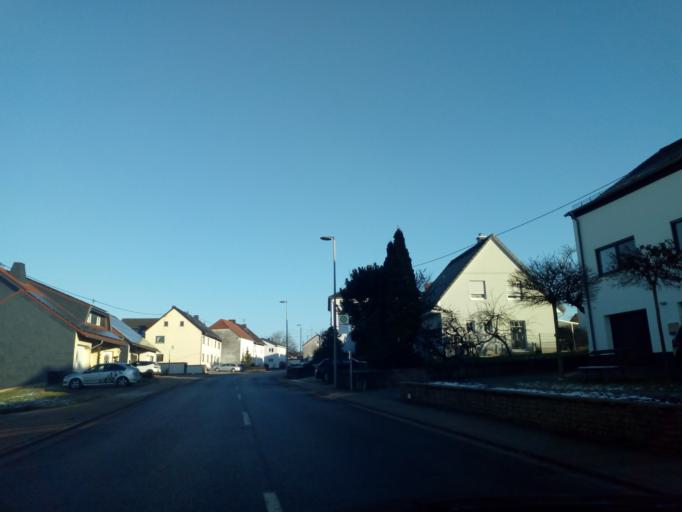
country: DE
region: Saarland
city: Heusweiler
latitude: 49.3620
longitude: 6.8896
